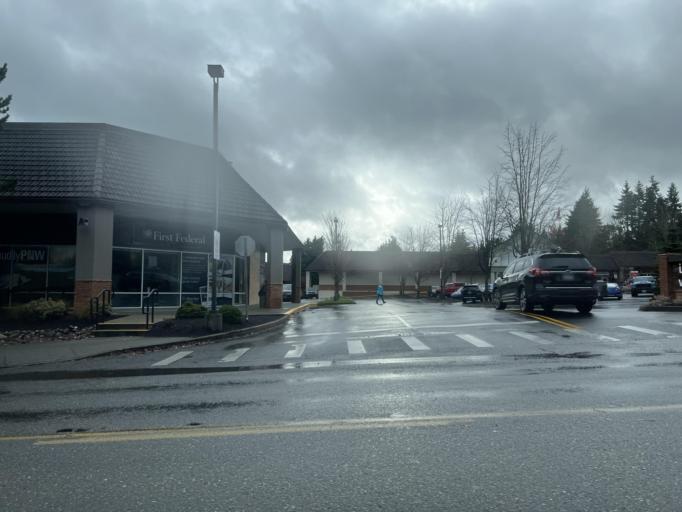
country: US
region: Washington
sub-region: Kitsap County
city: Bainbridge Island
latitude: 47.6358
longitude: -122.5179
